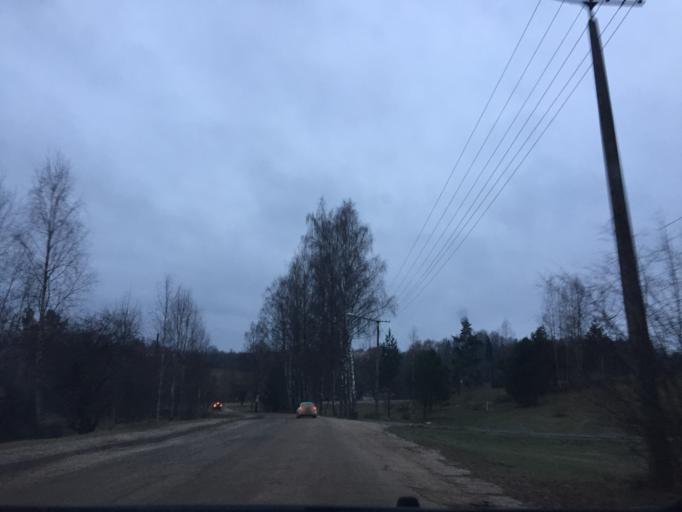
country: LV
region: Cesu Rajons
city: Cesis
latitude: 57.3245
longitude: 25.2570
